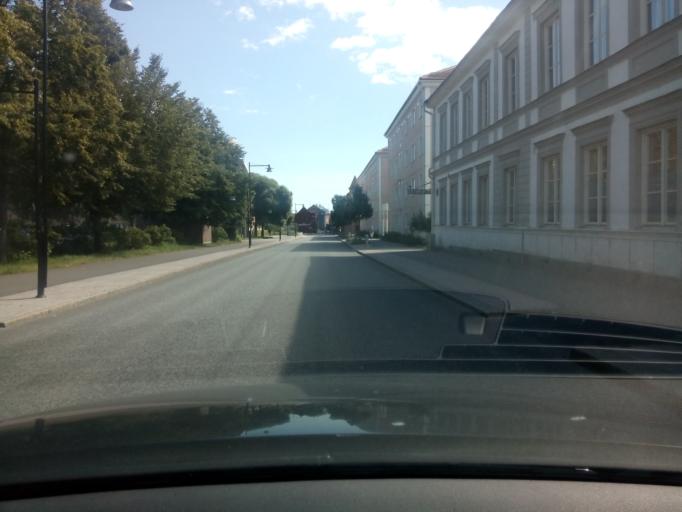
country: SE
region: Soedermanland
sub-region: Nykopings Kommun
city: Nykoping
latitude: 58.7499
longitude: 17.0142
